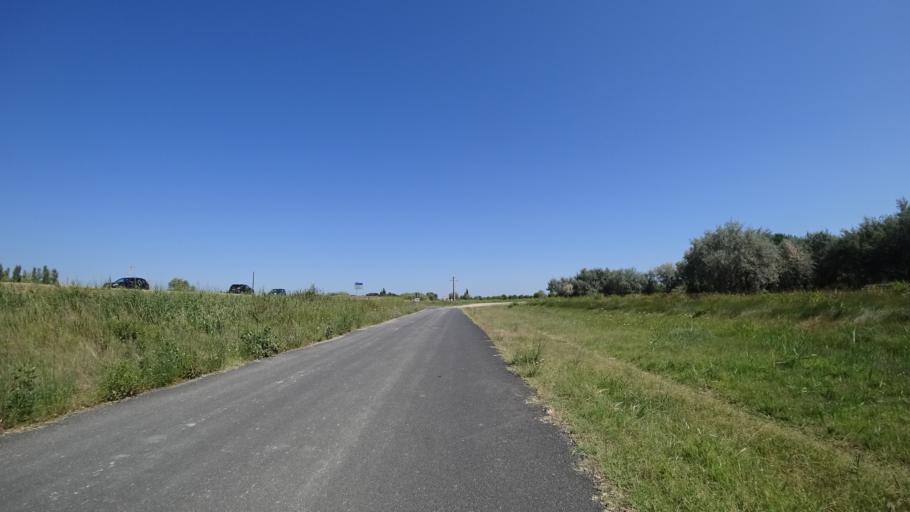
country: FR
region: Languedoc-Roussillon
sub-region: Departement des Pyrenees-Orientales
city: Sainte-Marie-Plage
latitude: 42.7362
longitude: 3.0254
